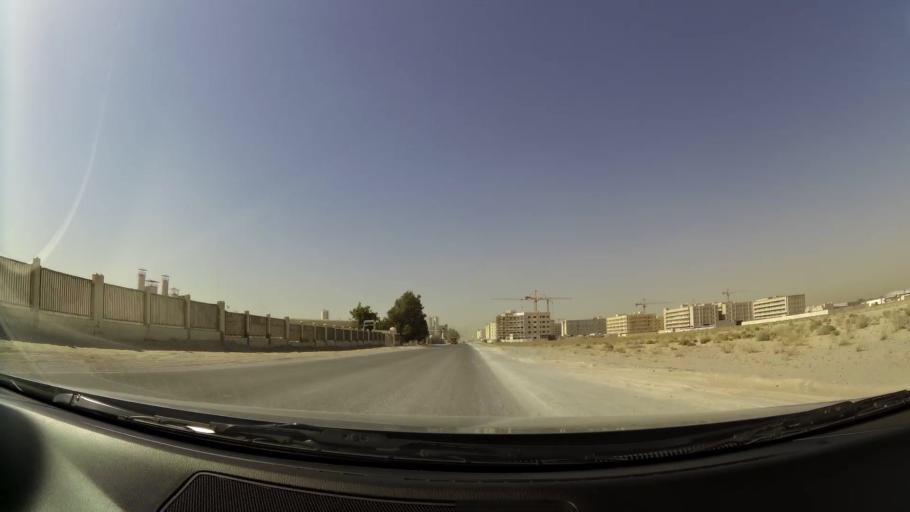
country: AE
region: Dubai
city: Dubai
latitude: 24.9893
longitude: 55.1389
